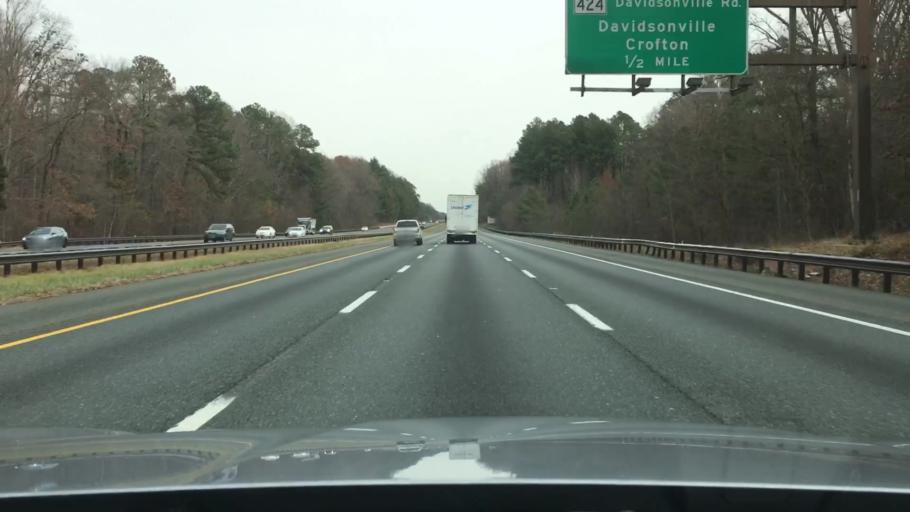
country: US
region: Maryland
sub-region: Anne Arundel County
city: Crofton
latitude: 38.9571
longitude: -76.6715
